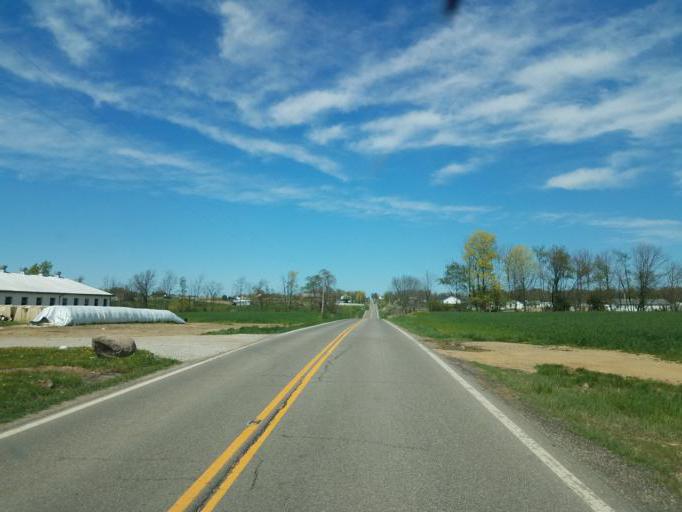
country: US
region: Ohio
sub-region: Ashland County
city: Ashland
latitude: 40.9059
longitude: -82.4115
